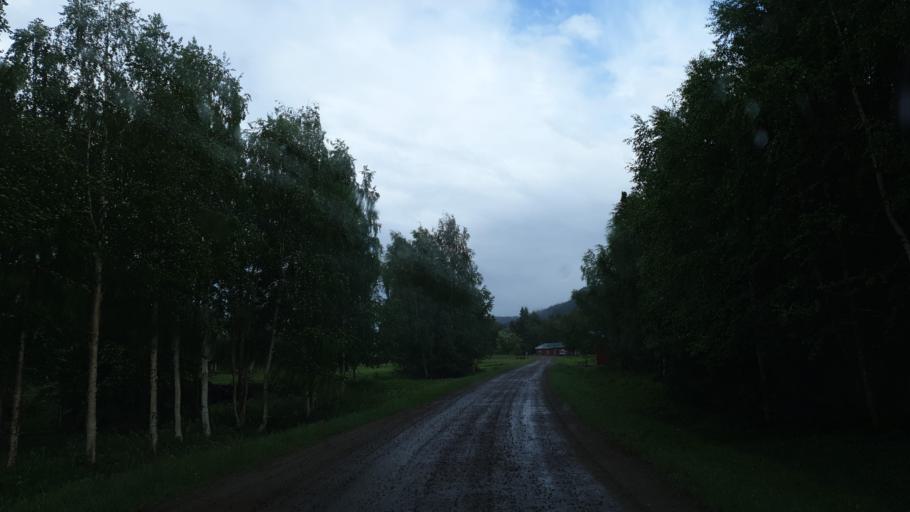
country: SE
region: Norrbotten
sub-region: Arvidsjaurs Kommun
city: Arvidsjaur
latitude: 65.7063
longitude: 18.7138
